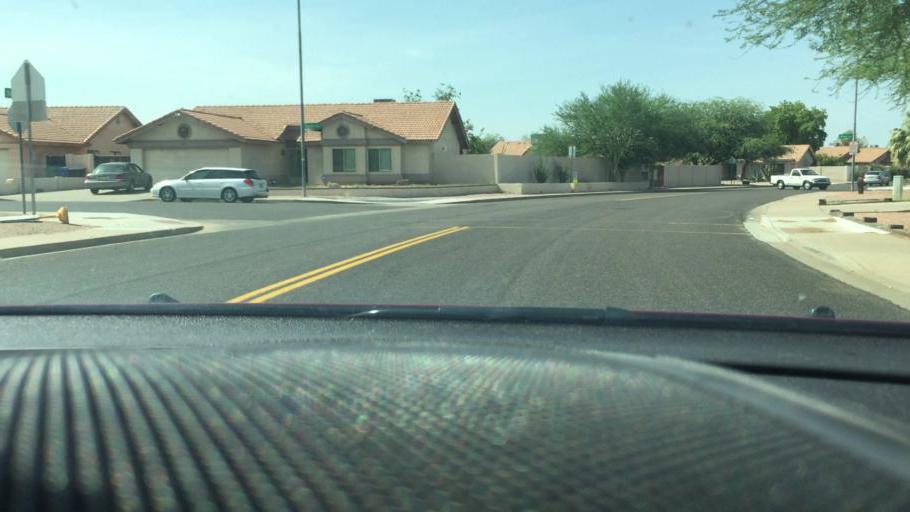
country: US
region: Arizona
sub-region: Maricopa County
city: Gilbert
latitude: 33.3998
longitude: -111.7140
